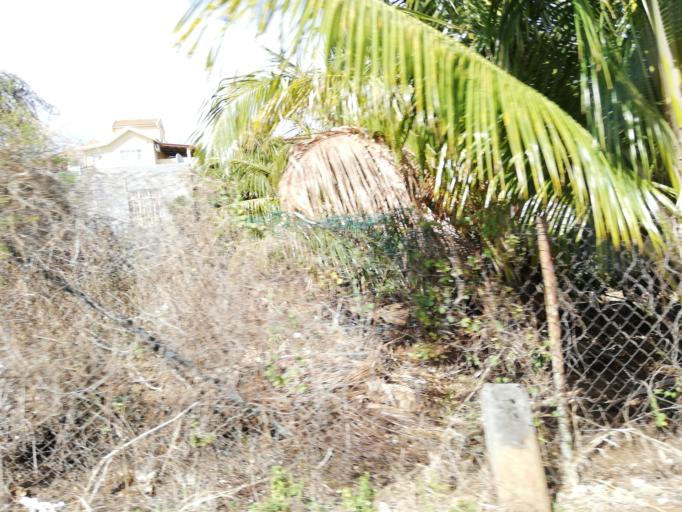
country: MU
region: Black River
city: Petite Riviere
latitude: -20.1950
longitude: 57.4660
